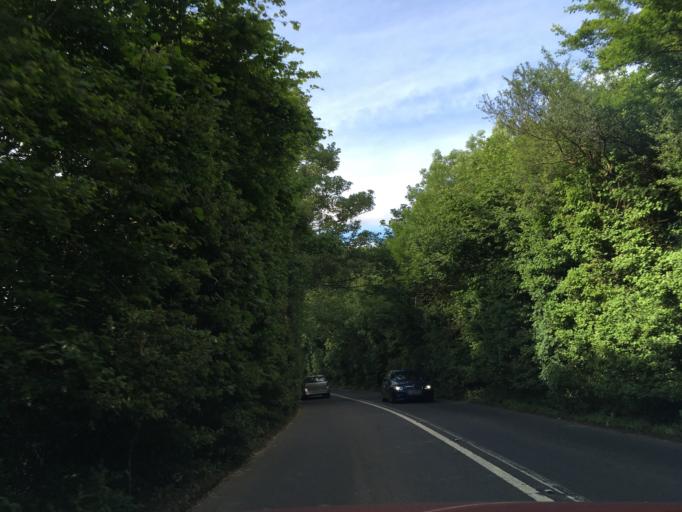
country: GB
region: England
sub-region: Devon
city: Newton Abbot
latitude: 50.5214
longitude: -3.6214
